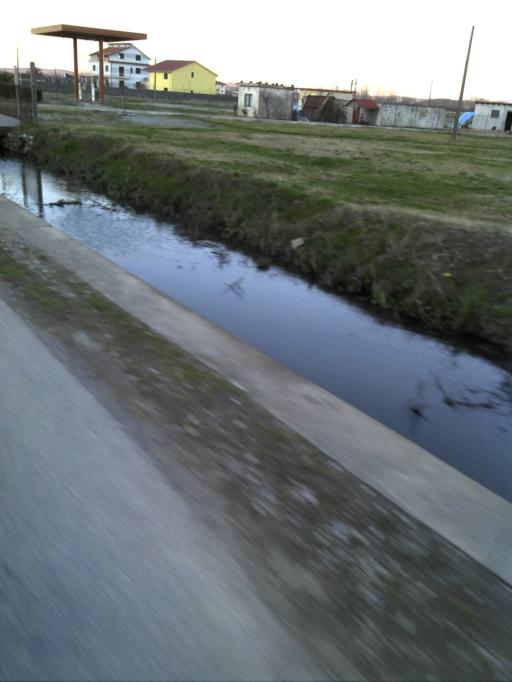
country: AL
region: Shkoder
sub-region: Rrethi i Shkodres
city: Berdica e Madhe
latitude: 42.0124
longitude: 19.4809
